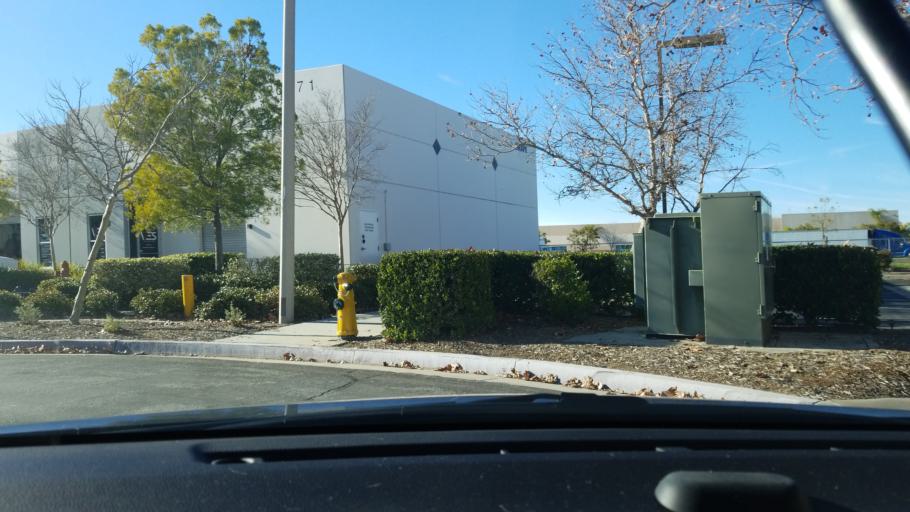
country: US
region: California
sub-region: Riverside County
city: Murrieta Hot Springs
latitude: 33.5332
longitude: -117.1813
